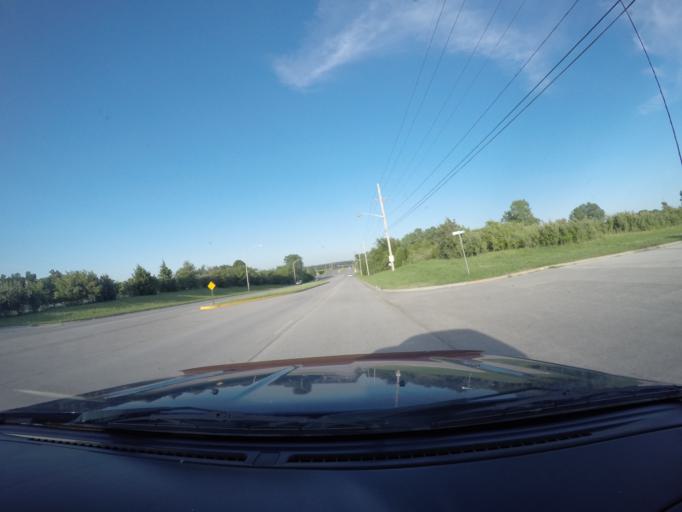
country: US
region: Kansas
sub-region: Wyandotte County
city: Edwardsville
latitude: 39.1430
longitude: -94.8113
